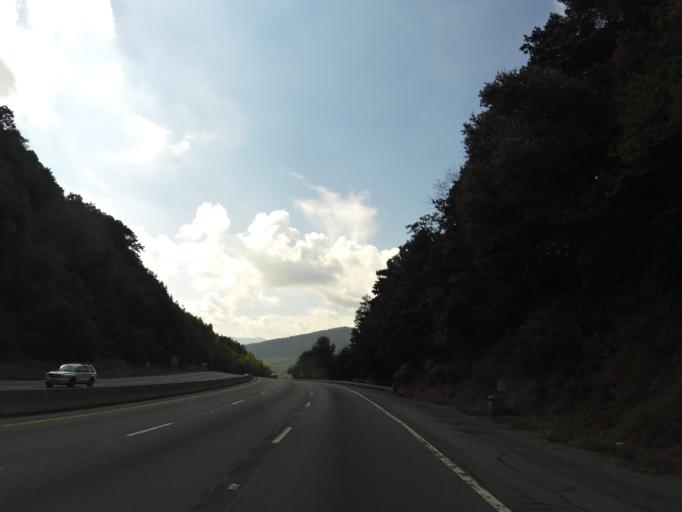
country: US
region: North Carolina
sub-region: Buncombe County
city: Black Mountain
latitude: 35.6186
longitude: -82.2632
